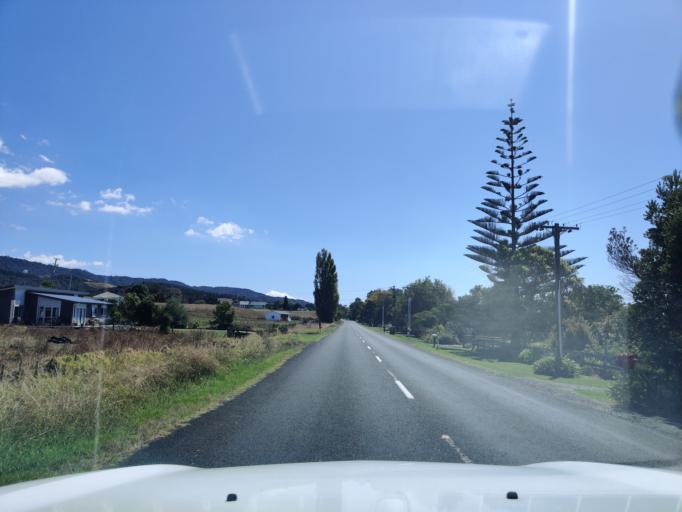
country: NZ
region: Waikato
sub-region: Thames-Coromandel District
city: Thames
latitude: -37.0475
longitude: 175.2991
